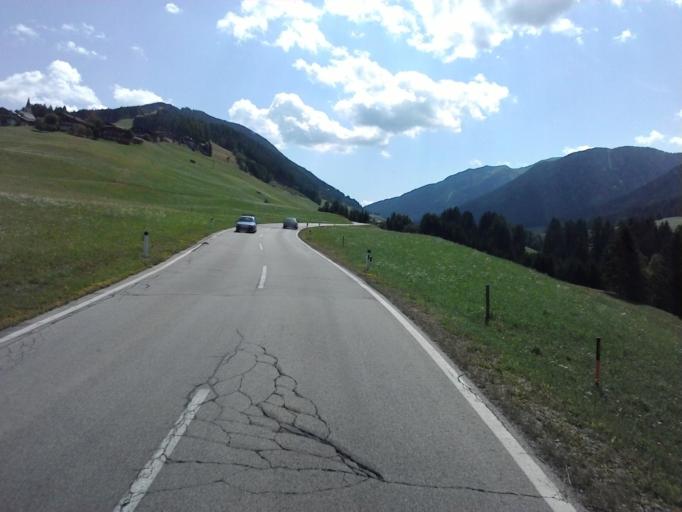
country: AT
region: Tyrol
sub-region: Politischer Bezirk Lienz
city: Strassen
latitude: 46.7374
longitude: 12.4716
